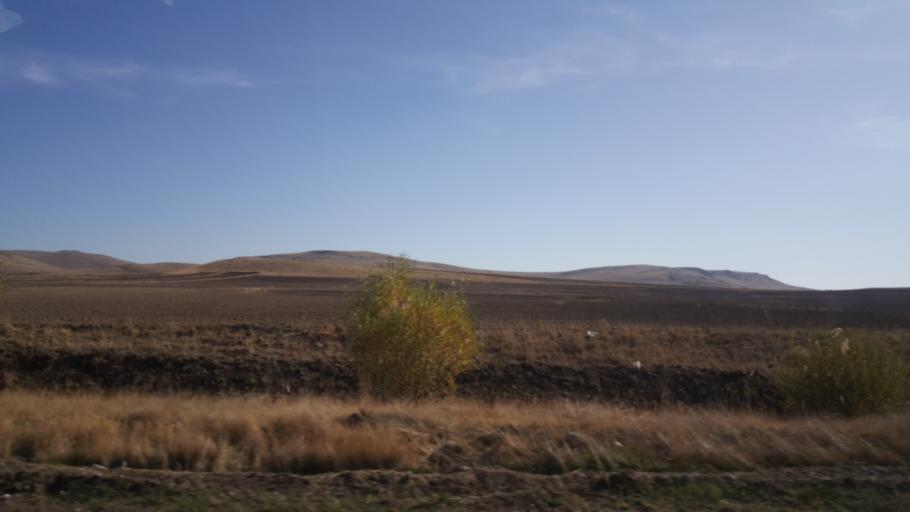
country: TR
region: Ankara
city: Yenice
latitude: 39.3578
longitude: 32.7966
